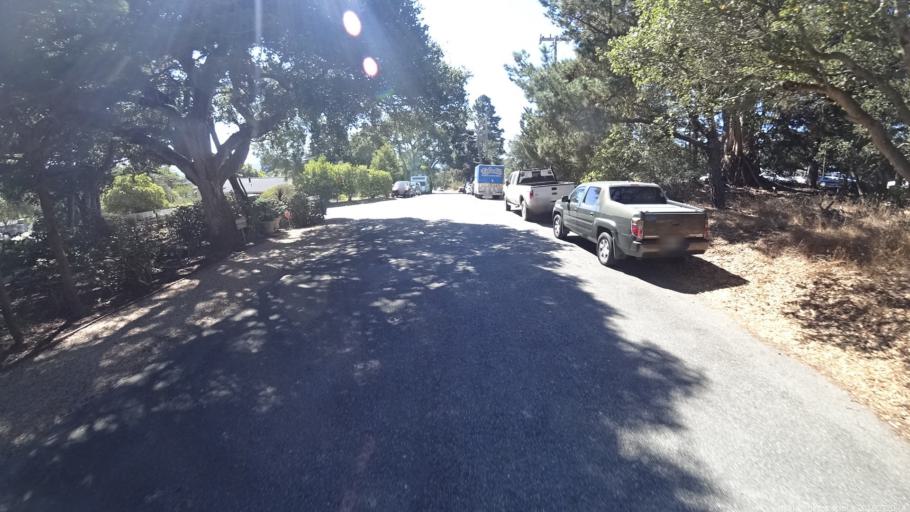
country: US
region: California
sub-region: Monterey County
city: Carmel-by-the-Sea
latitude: 36.5600
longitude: -121.9112
